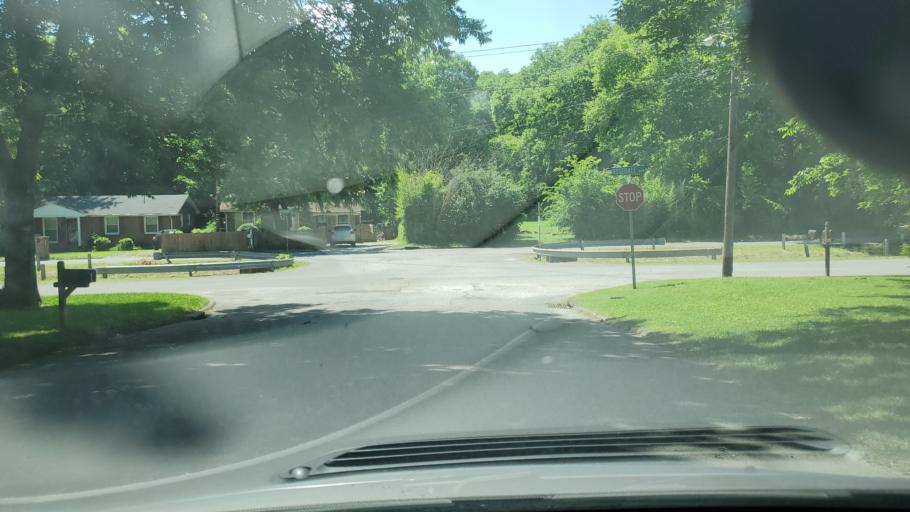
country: US
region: Tennessee
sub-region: Davidson County
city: Nashville
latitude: 36.1973
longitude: -86.7564
